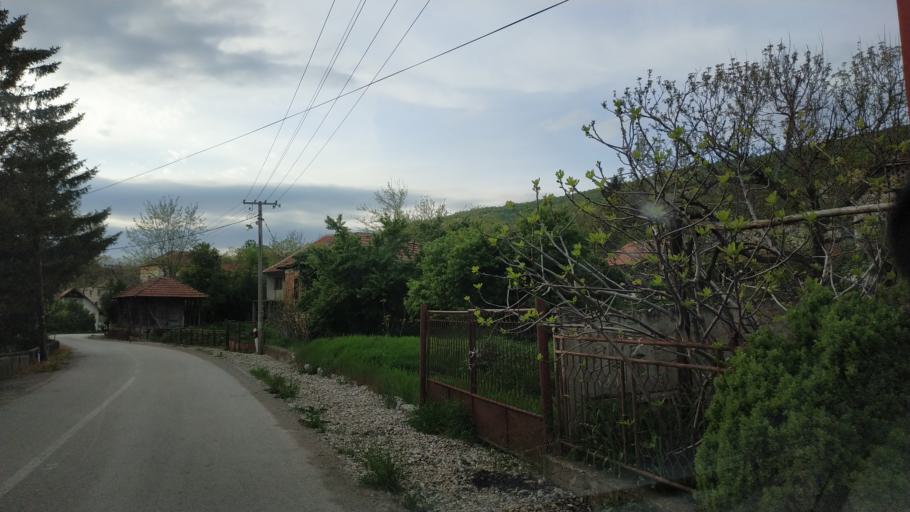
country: RS
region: Central Serbia
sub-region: Zajecarski Okrug
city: Soko Banja
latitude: 43.5272
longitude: 21.8560
